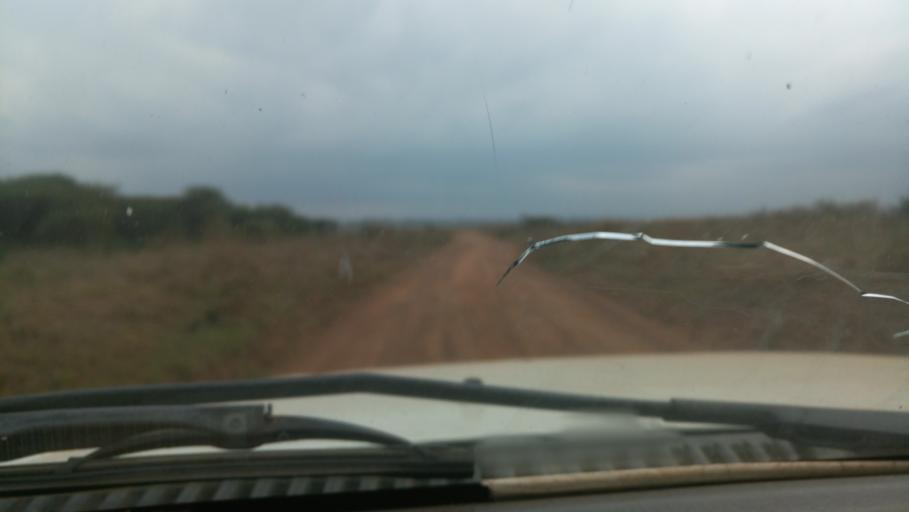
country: KE
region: Nairobi Area
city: Nairobi
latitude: -1.3469
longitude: 36.8183
